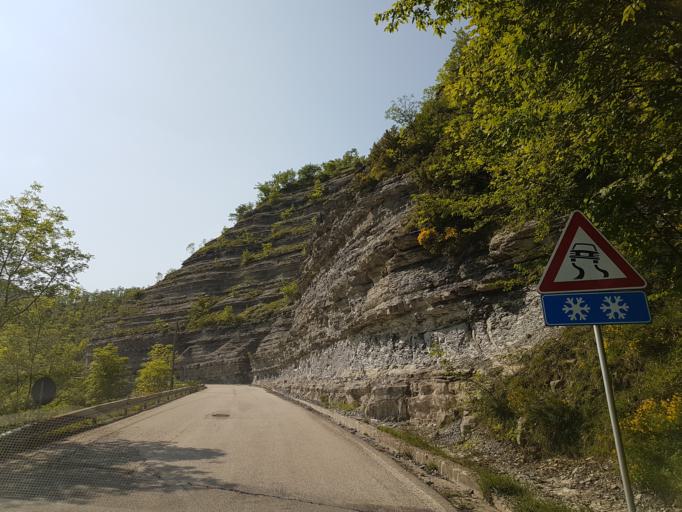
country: IT
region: Emilia-Romagna
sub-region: Forli-Cesena
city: San Piero in Bagno
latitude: 43.8112
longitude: 11.9302
